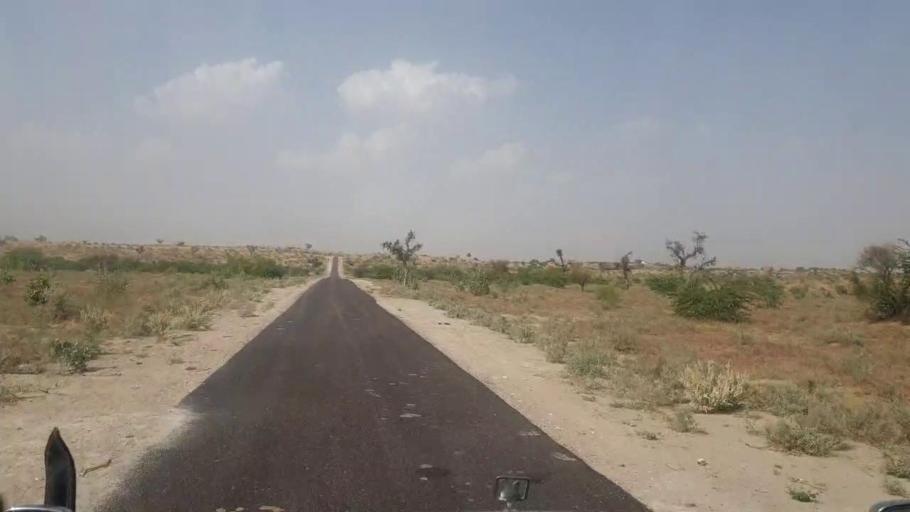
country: PK
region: Sindh
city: Islamkot
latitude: 25.2057
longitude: 70.2834
